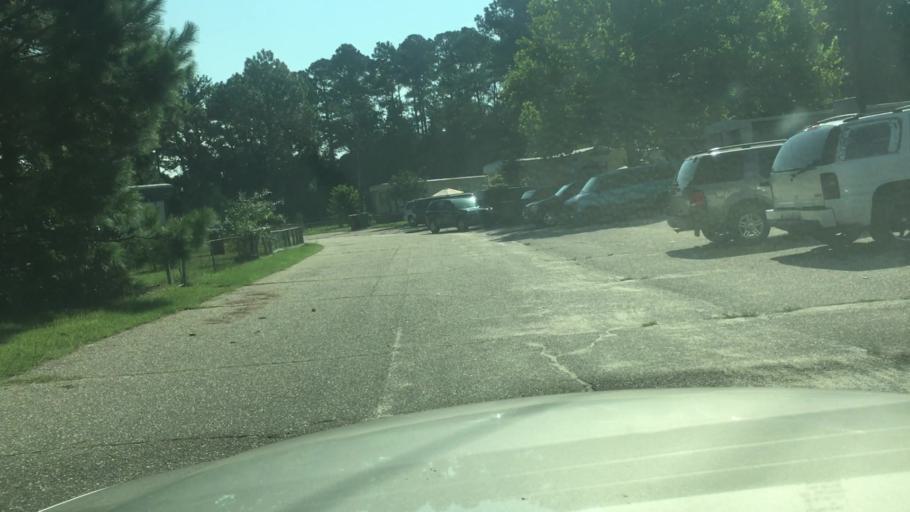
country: US
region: North Carolina
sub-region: Cumberland County
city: Spring Lake
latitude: 35.1503
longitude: -78.9105
